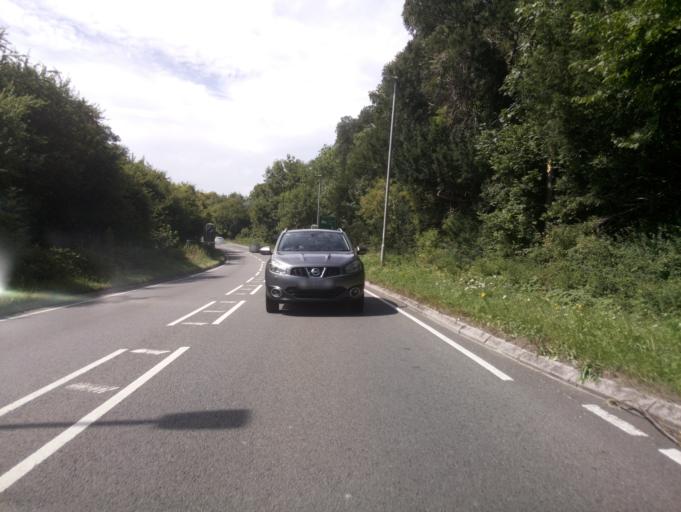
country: GB
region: England
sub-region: Dorset
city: Dorchester
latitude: 50.7492
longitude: -2.5123
